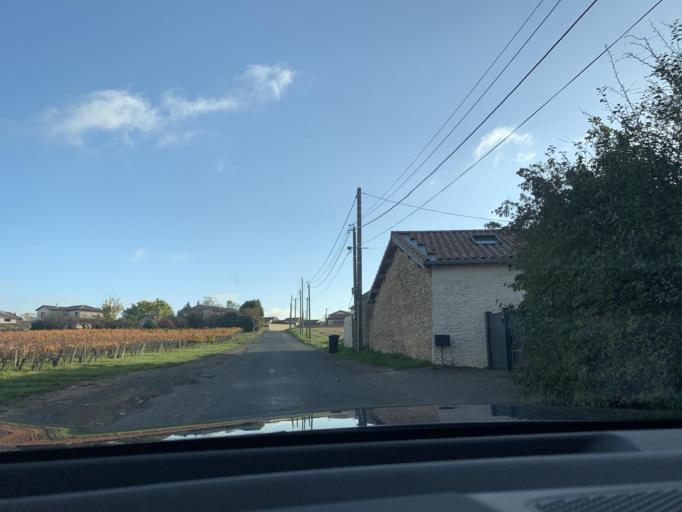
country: FR
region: Rhone-Alpes
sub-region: Departement du Rhone
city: Liergues
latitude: 45.9481
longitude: 4.6690
